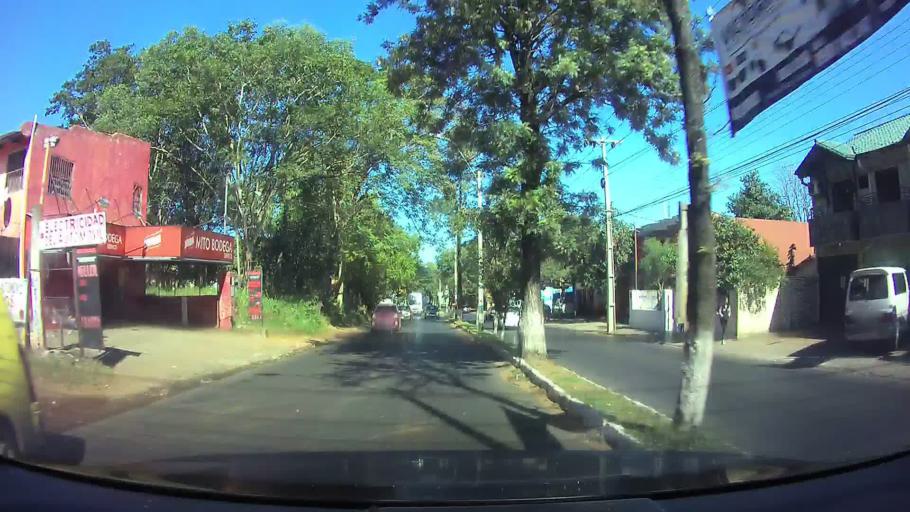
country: PY
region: Central
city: Villa Elisa
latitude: -25.3628
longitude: -57.5767
